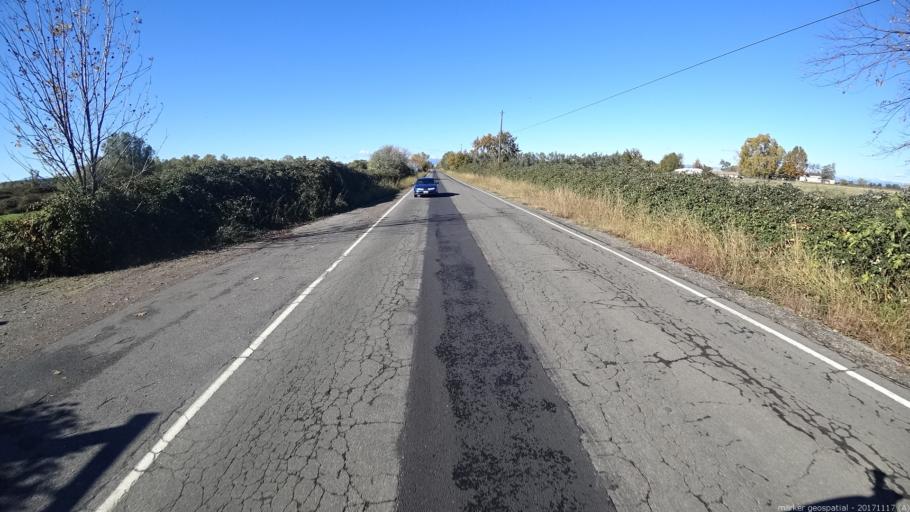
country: US
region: California
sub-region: Shasta County
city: Anderson
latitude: 40.4303
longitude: -122.2519
